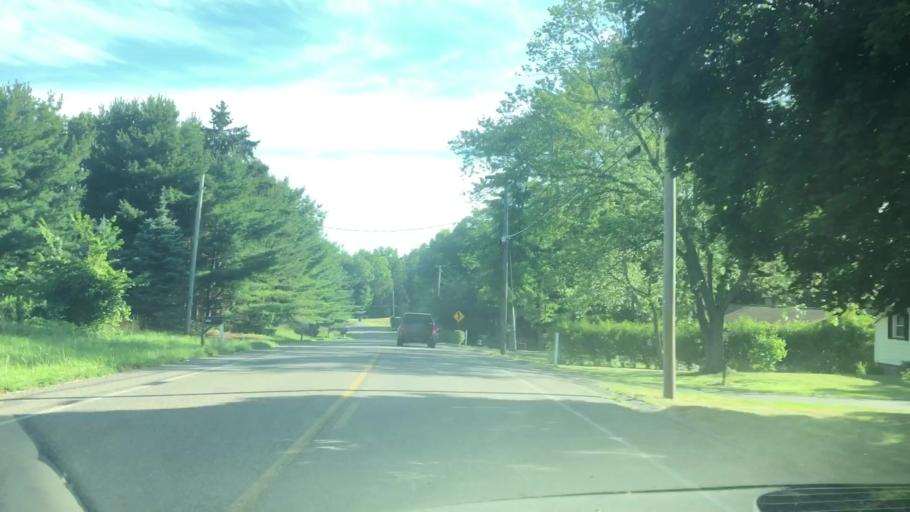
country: US
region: New York
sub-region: Wayne County
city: Macedon
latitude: 43.0493
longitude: -77.3370
